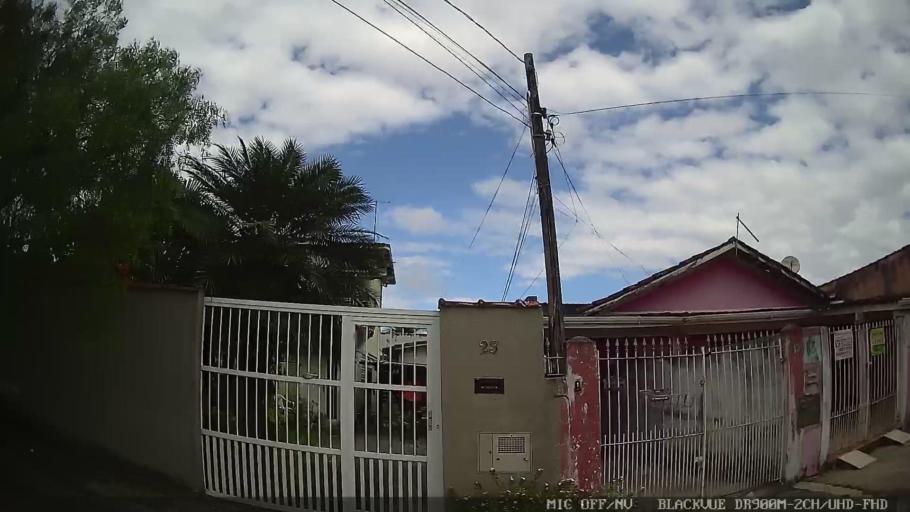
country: BR
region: Sao Paulo
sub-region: Caraguatatuba
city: Caraguatatuba
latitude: -23.6386
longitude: -45.4356
